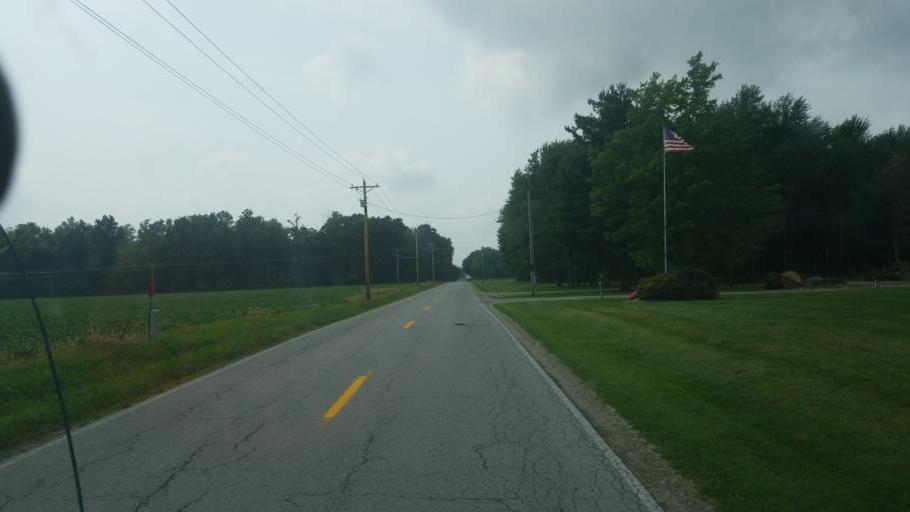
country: US
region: Ohio
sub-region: Huron County
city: Greenwich
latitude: 41.0520
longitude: -82.5334
